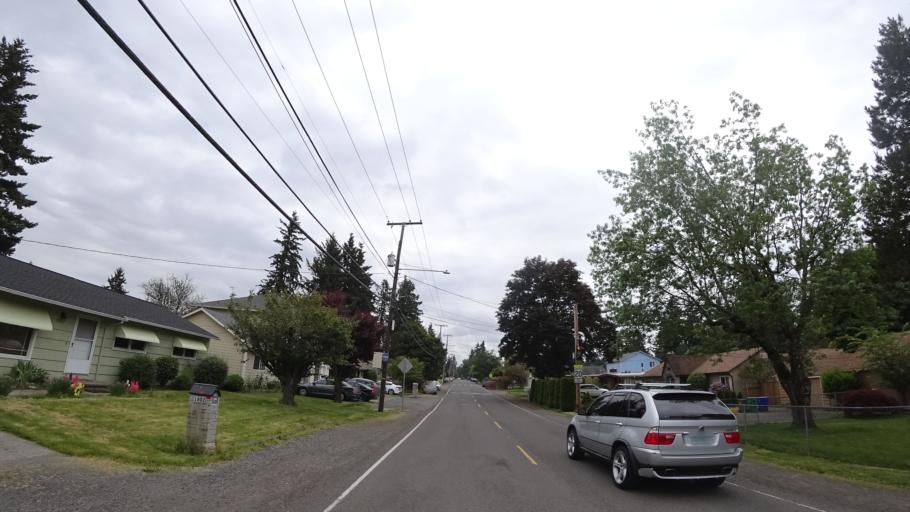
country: US
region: Oregon
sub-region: Multnomah County
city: Lents
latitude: 45.5106
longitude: -122.5428
